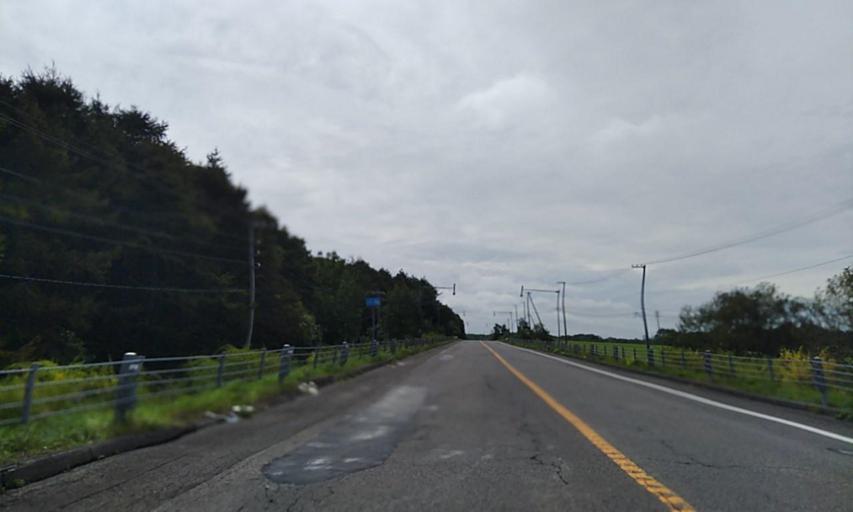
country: JP
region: Hokkaido
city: Shibetsu
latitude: 43.6204
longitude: 145.1805
